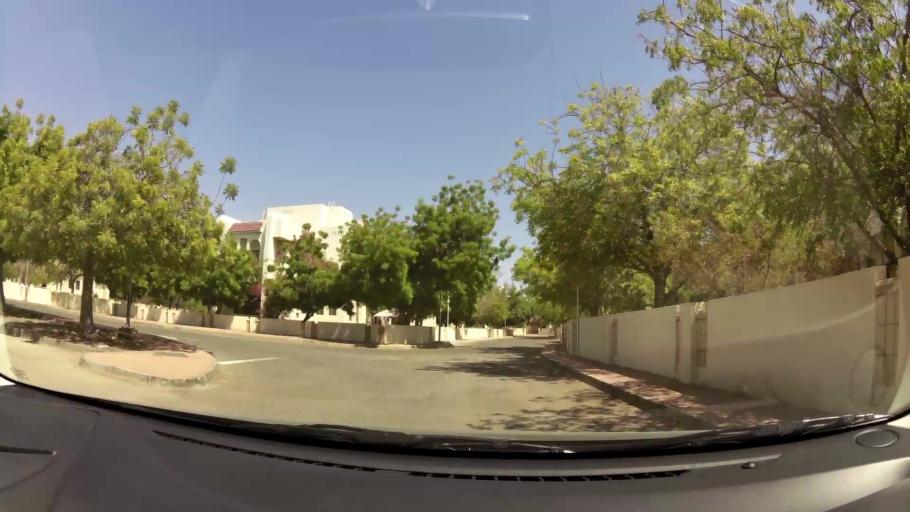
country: OM
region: Muhafazat Masqat
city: As Sib al Jadidah
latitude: 23.6163
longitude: 58.2462
